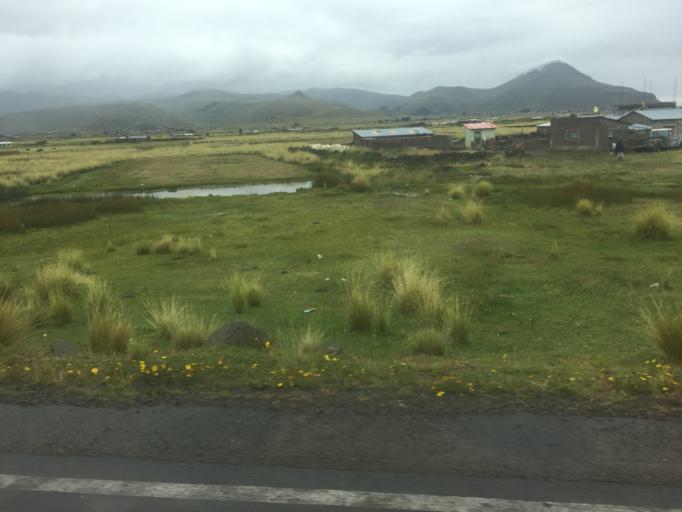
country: PE
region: Puno
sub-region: Provincia de Chucuito
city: Pomata
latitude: -16.3171
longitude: -69.2564
